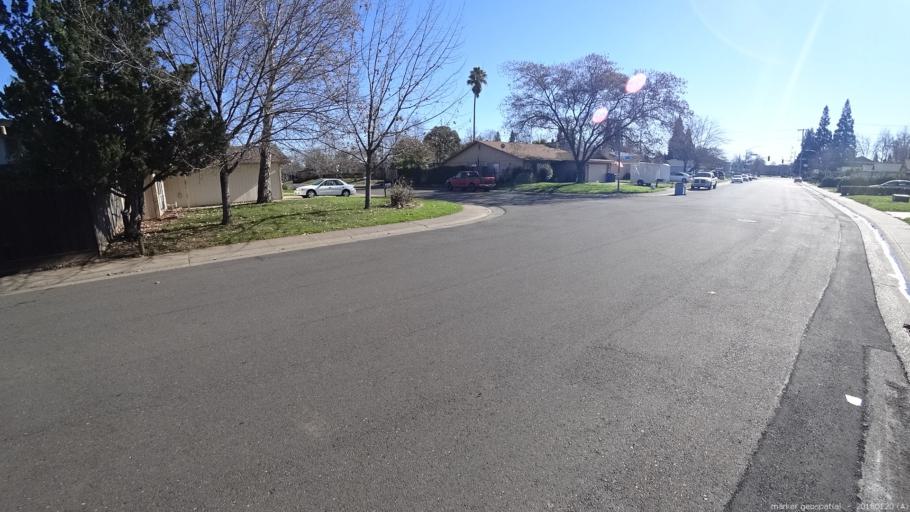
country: US
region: California
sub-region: Sacramento County
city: La Riviera
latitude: 38.5587
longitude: -121.3309
